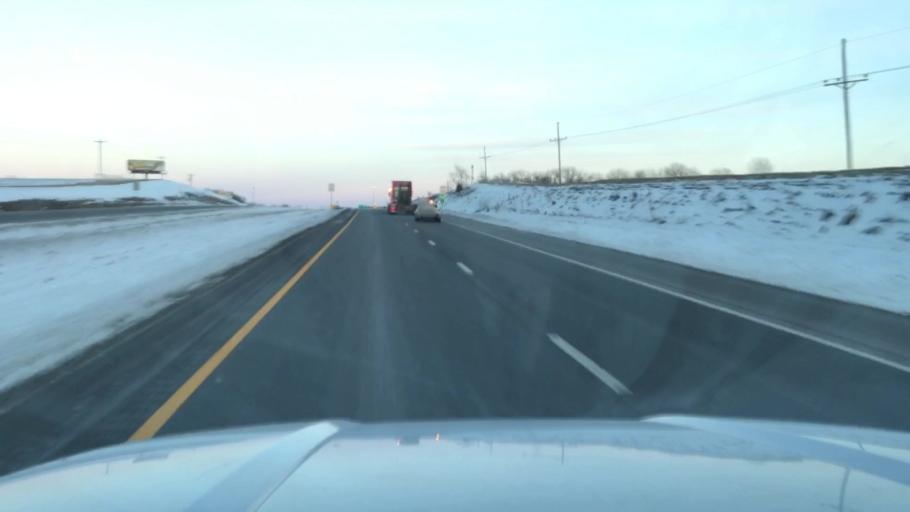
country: US
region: Missouri
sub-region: Clinton County
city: Cameron
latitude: 39.7538
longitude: -94.2611
